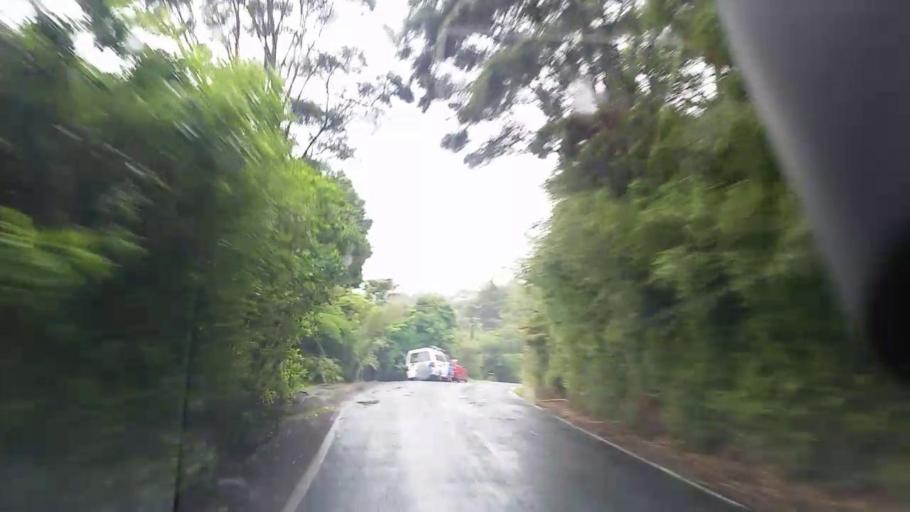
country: NZ
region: Auckland
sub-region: Auckland
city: Waitakere
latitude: -36.9044
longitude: 174.5720
